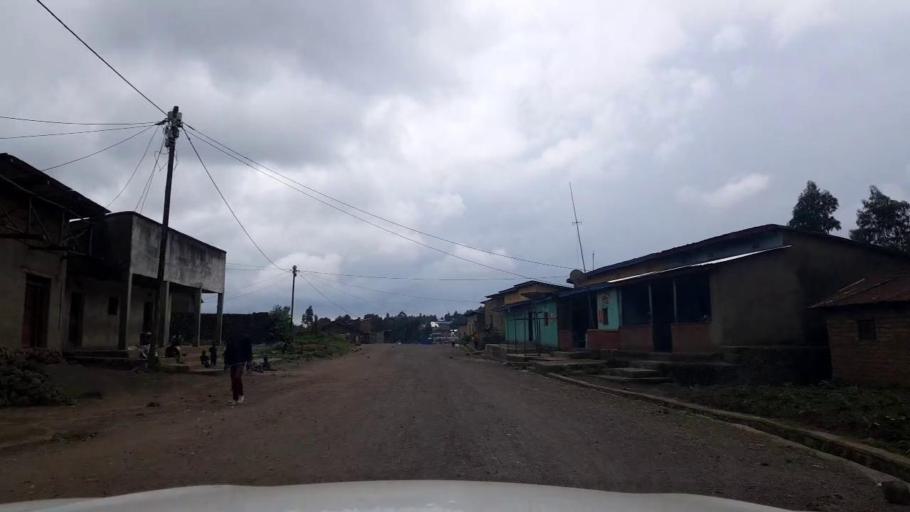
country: RW
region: Northern Province
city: Musanze
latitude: -1.5811
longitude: 29.4798
